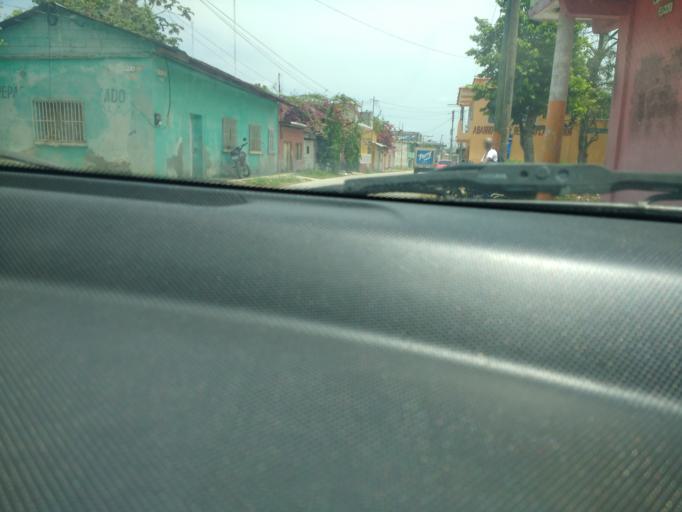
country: GT
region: Peten
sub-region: Municipio de Flores
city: Flores
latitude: 16.9245
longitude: -89.9013
